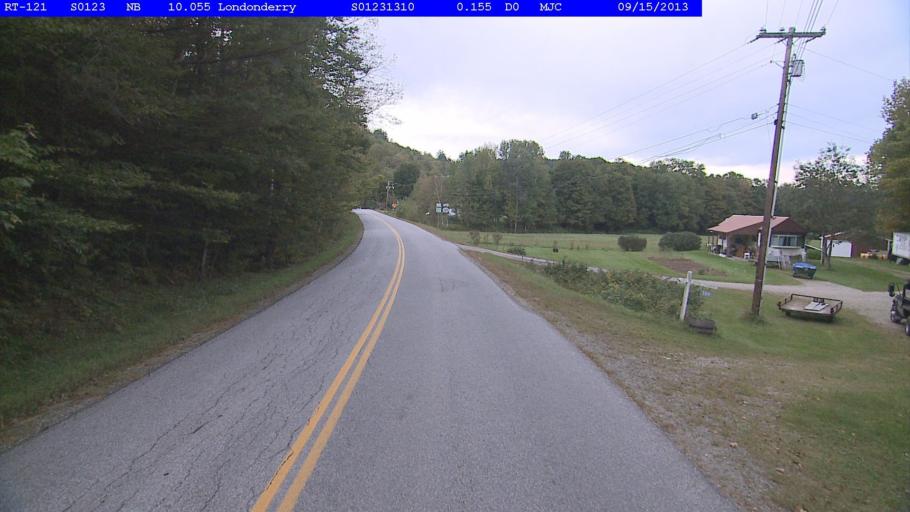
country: US
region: Vermont
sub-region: Windsor County
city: Chester
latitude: 43.2153
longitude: -72.7386
